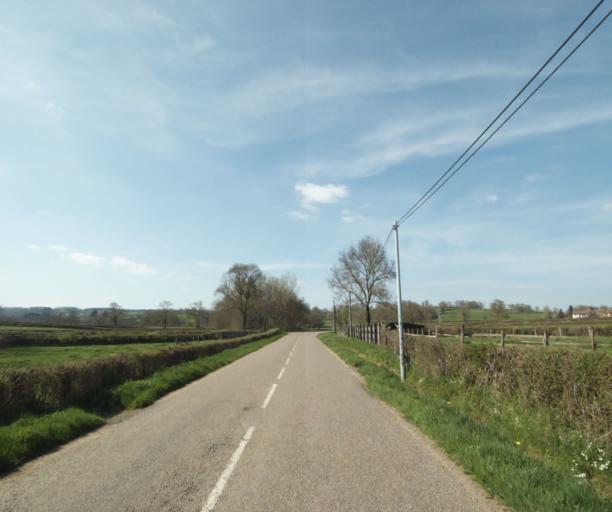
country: FR
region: Bourgogne
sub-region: Departement de Saone-et-Loire
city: Charolles
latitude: 46.3876
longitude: 4.3477
